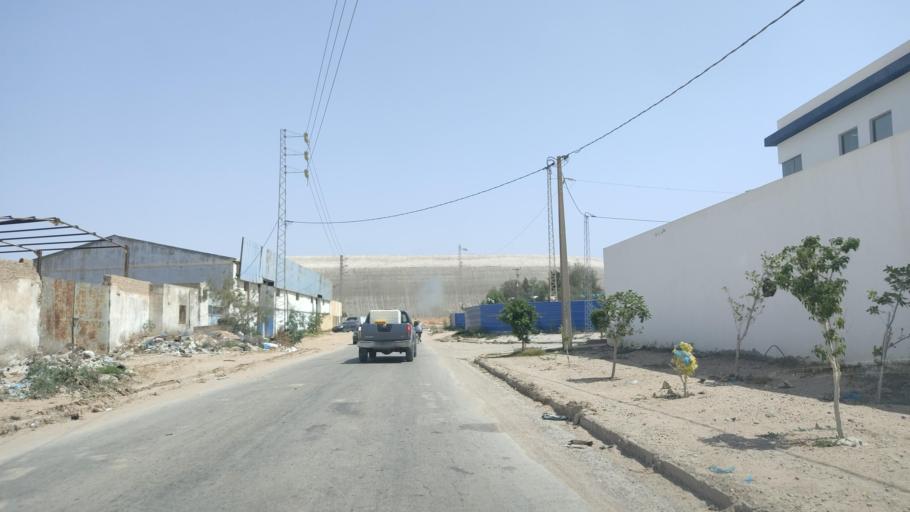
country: TN
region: Safaqis
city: Sfax
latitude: 34.6916
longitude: 10.7265
